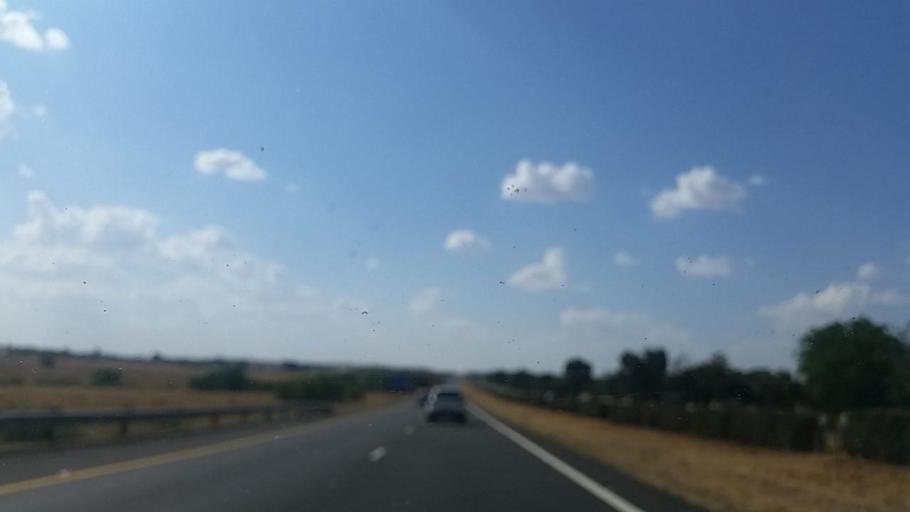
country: ZA
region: Orange Free State
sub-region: Mangaung Metropolitan Municipality
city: Bloemfontein
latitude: -29.1776
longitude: 26.1882
